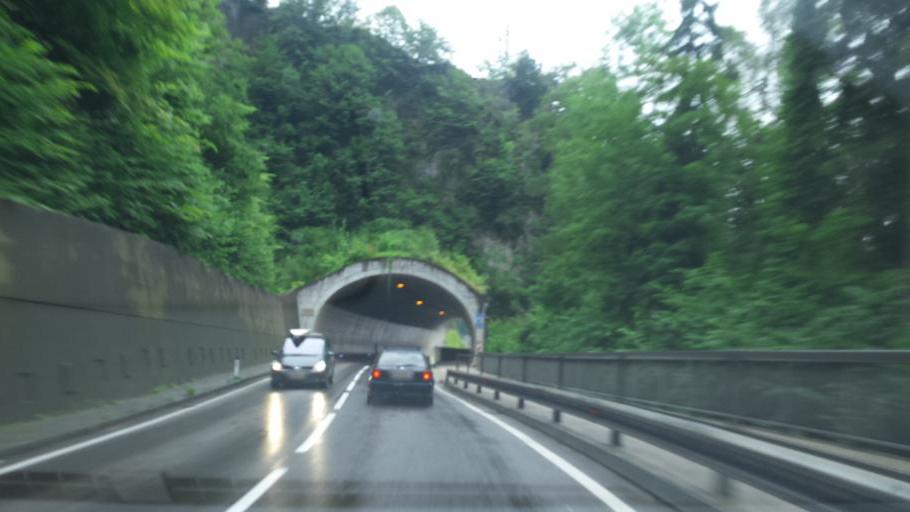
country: AT
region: Upper Austria
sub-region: Politischer Bezirk Gmunden
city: Ebensee
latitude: 47.8333
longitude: 13.7854
